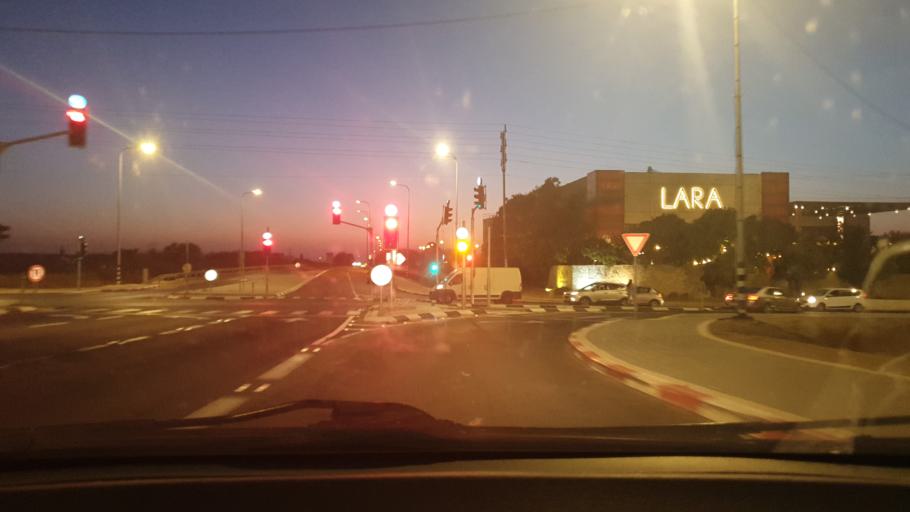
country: IL
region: Central District
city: Bene 'Ayish
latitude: 31.7960
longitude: 34.7610
